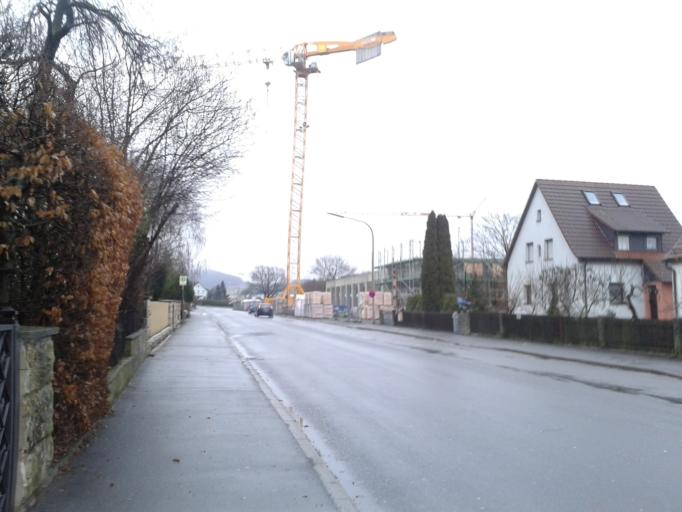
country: DE
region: Bavaria
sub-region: Upper Franconia
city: Kronach
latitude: 50.2351
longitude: 11.3346
